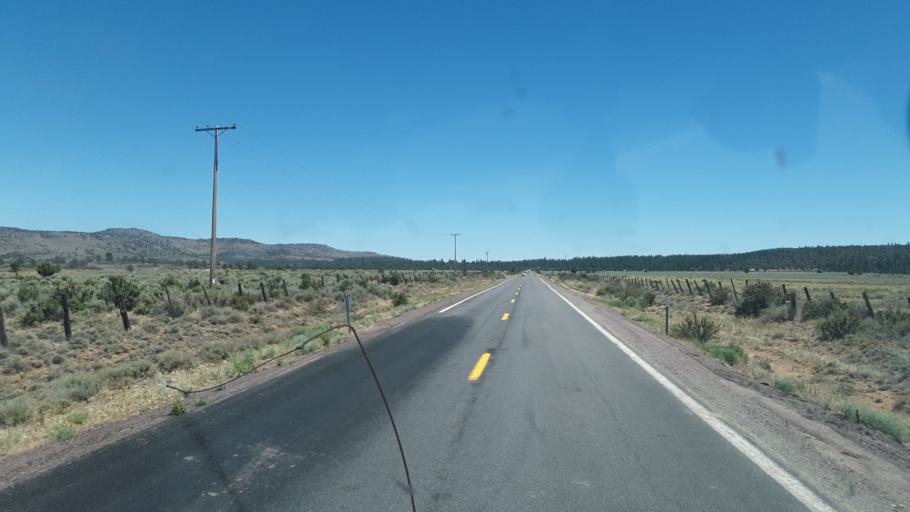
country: US
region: California
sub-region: Lassen County
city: Susanville
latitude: 40.5308
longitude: -120.6041
